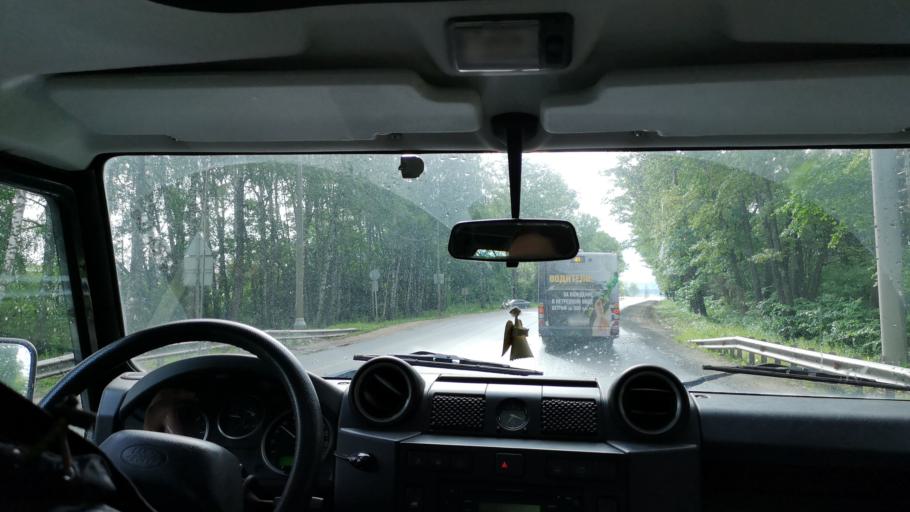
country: RU
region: Moskovskaya
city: Gorshkovo
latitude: 56.3675
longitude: 37.4598
